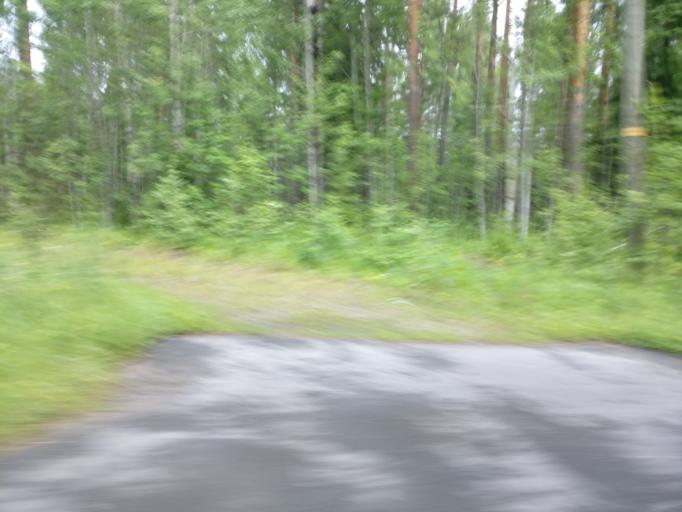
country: FI
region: Southern Savonia
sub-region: Pieksaemaeki
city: Joroinen
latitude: 62.1982
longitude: 27.9943
